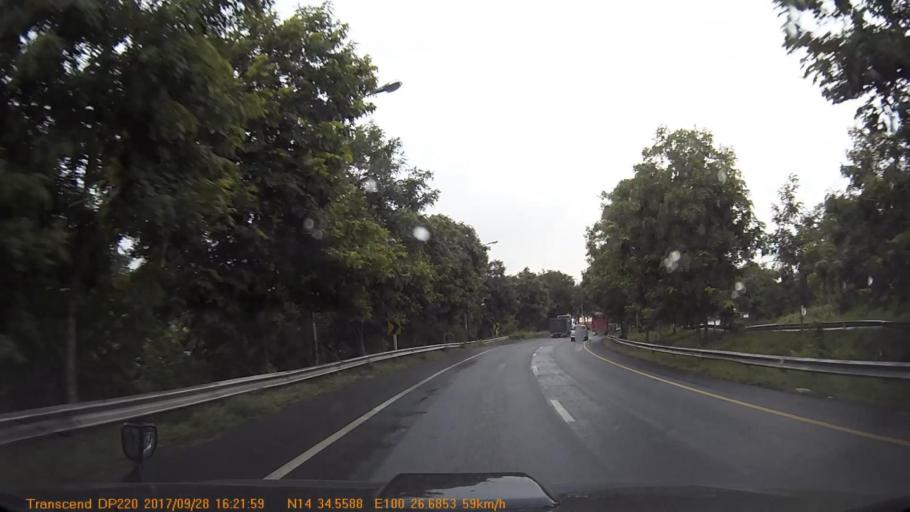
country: TH
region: Ang Thong
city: Ang Thong
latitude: 14.5764
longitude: 100.4441
